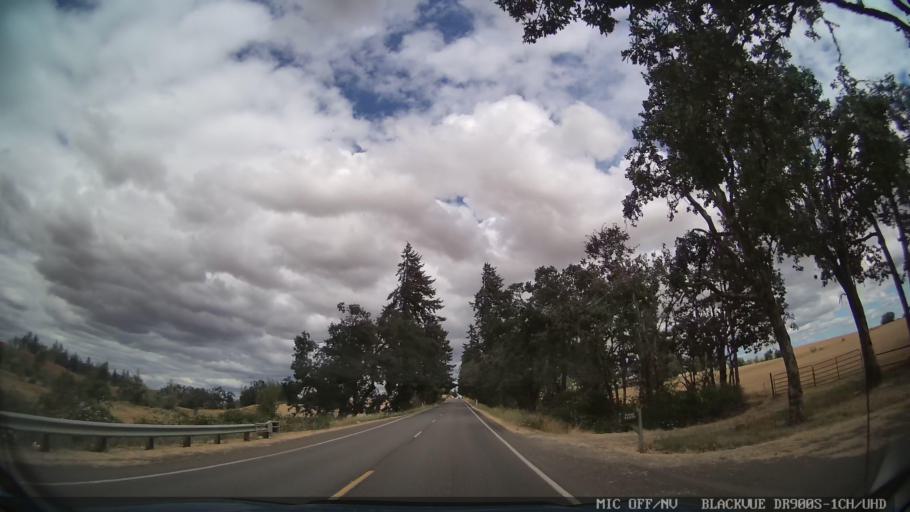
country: US
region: Oregon
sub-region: Marion County
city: Sublimity
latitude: 44.8655
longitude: -122.8236
